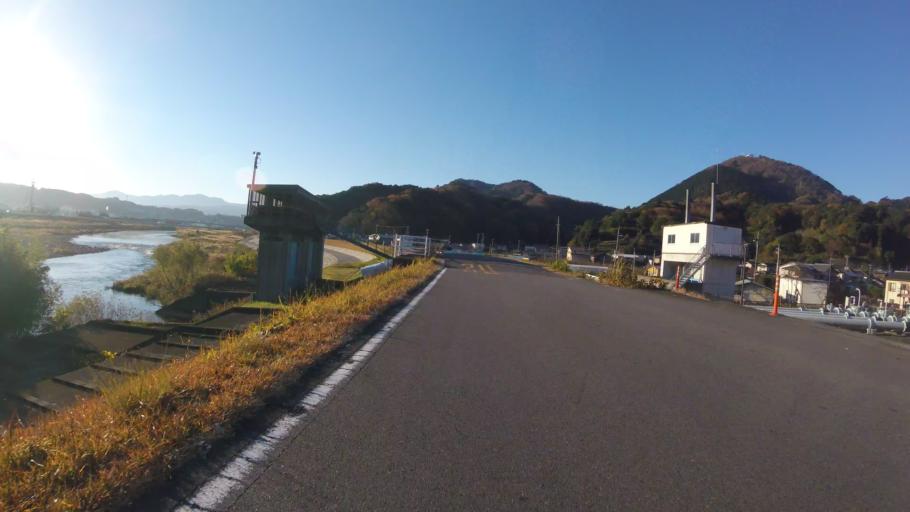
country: JP
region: Shizuoka
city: Mishima
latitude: 35.0207
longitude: 138.9364
